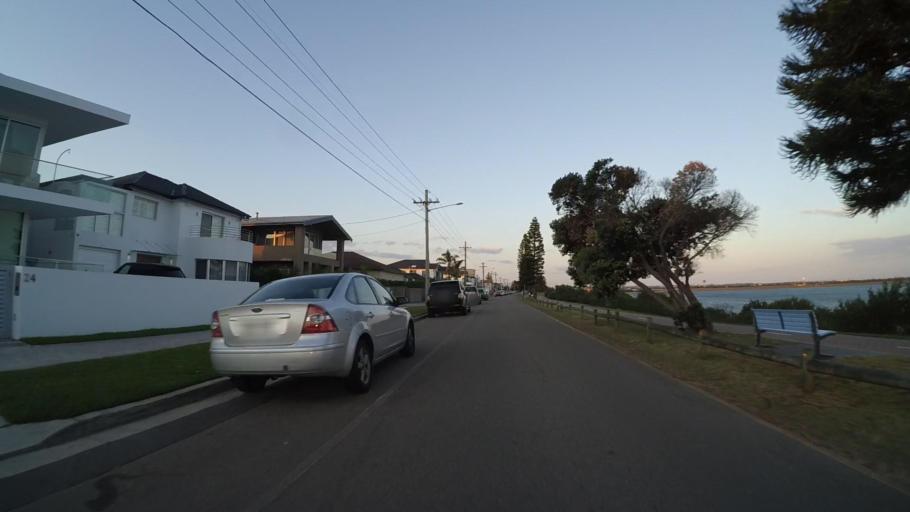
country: AU
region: New South Wales
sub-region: Rockdale
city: Brighton-Le-Sands
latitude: -33.9544
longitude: 151.1604
